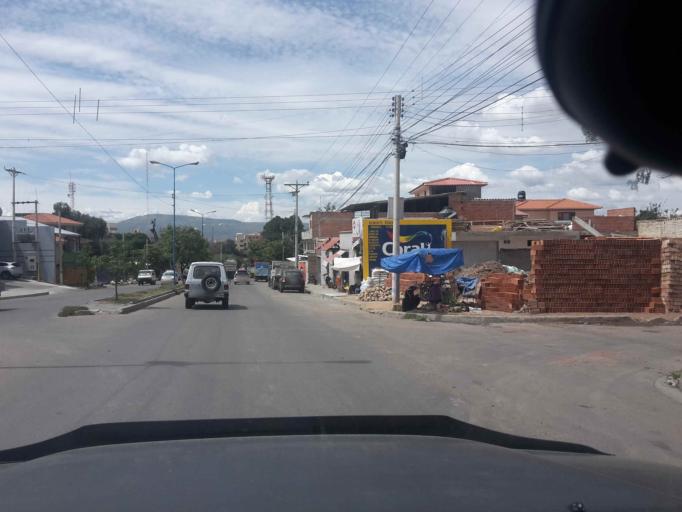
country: BO
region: Cochabamba
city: Cochabamba
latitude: -17.3600
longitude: -66.1725
